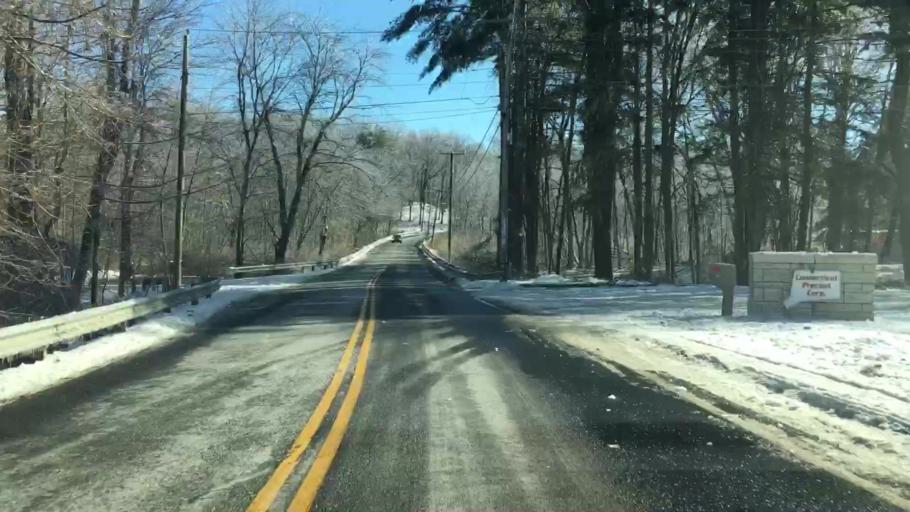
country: US
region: Connecticut
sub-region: Fairfield County
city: Newtown
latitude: 41.3592
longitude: -73.2385
